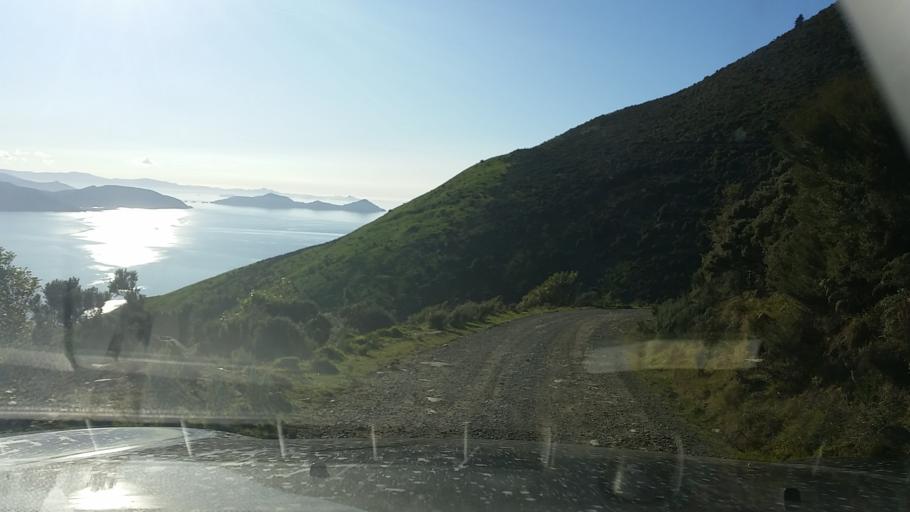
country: NZ
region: Marlborough
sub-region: Marlborough District
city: Picton
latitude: -41.0220
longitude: 174.1599
